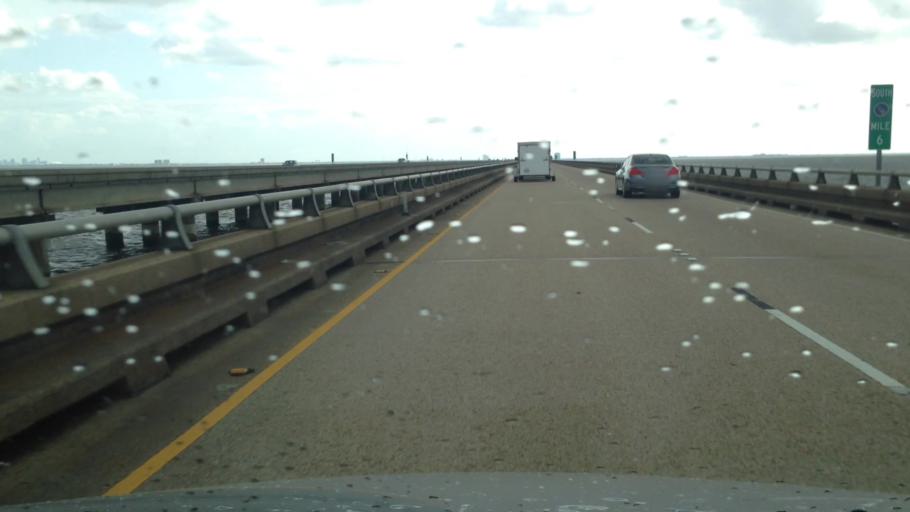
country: US
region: Louisiana
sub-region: Jefferson Parish
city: Metairie
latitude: 30.1080
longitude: -90.1391
